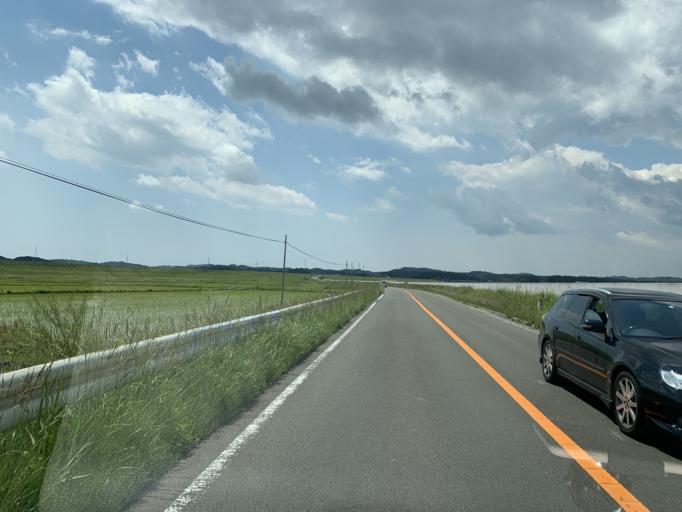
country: JP
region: Miyagi
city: Matsushima
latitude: 38.4476
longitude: 141.0809
